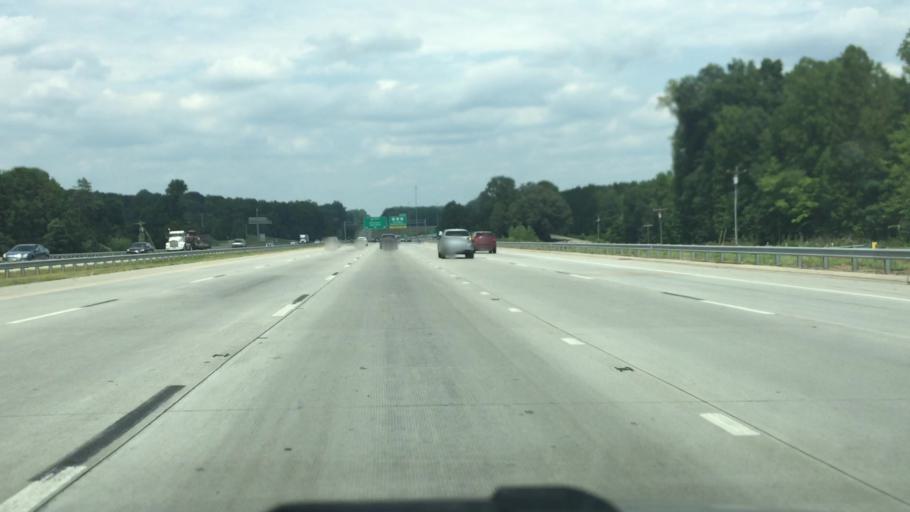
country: US
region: North Carolina
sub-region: Davidson County
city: Tyro
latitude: 35.7654
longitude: -80.3342
